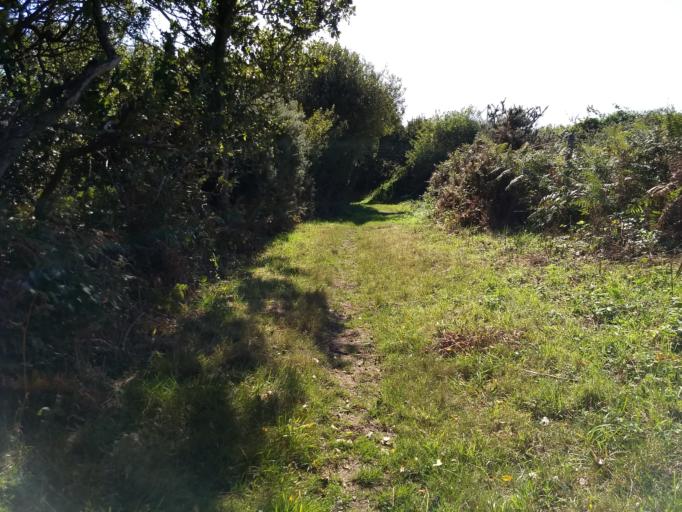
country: GB
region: England
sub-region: Isle of Wight
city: Niton
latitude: 50.6347
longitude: -1.2764
